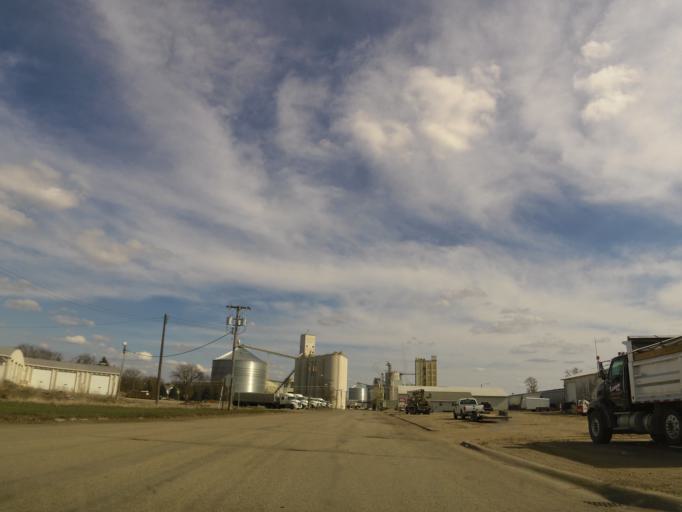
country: US
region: Minnesota
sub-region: Lac qui Parle County
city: Dawson
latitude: 44.9352
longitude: -96.0623
